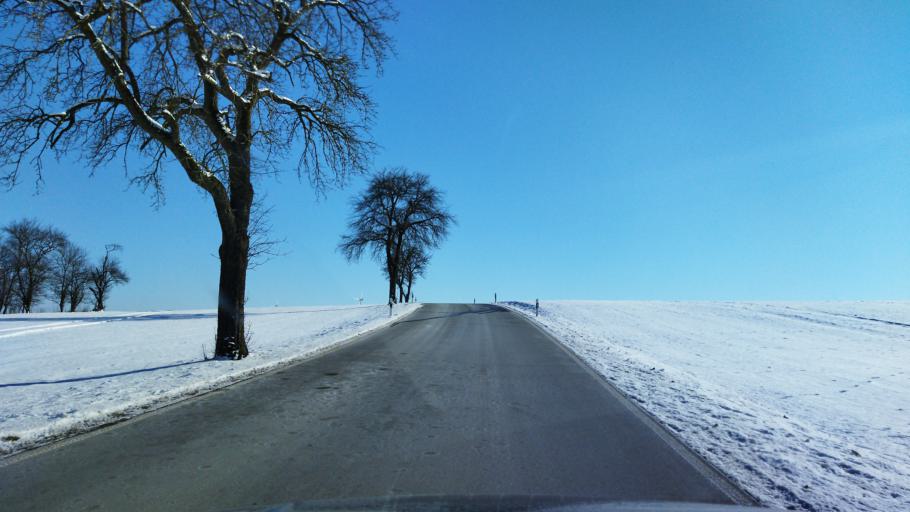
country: DE
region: Baden-Wuerttemberg
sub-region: Regierungsbezirk Stuttgart
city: Ilshofen
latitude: 49.2055
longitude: 9.9250
